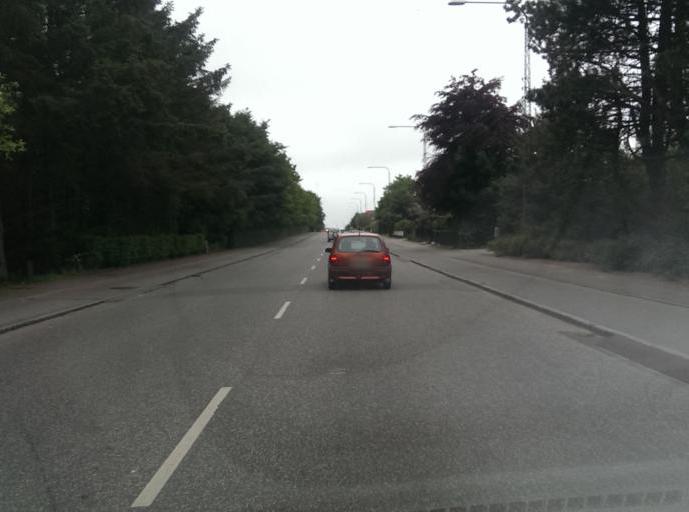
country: DK
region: South Denmark
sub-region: Fano Kommune
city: Nordby
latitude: 55.5177
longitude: 8.3657
